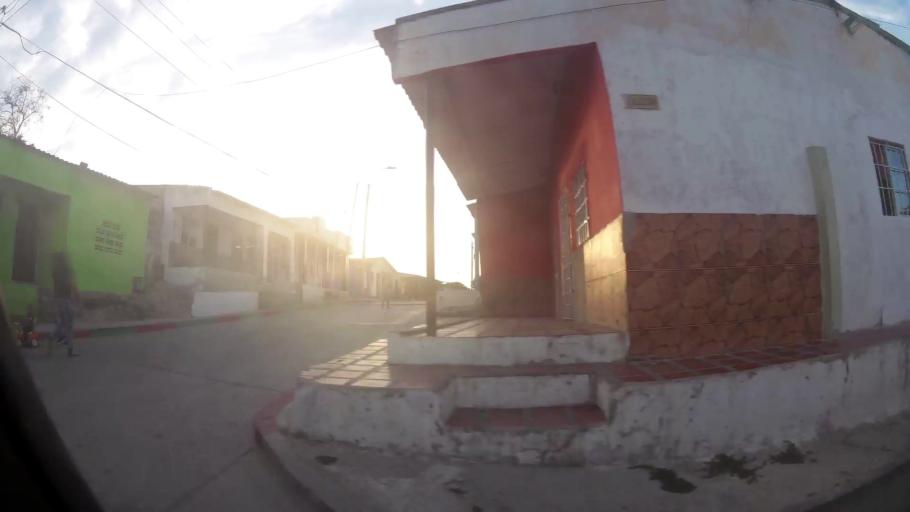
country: CO
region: Atlantico
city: Barranquilla
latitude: 10.9556
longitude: -74.8282
